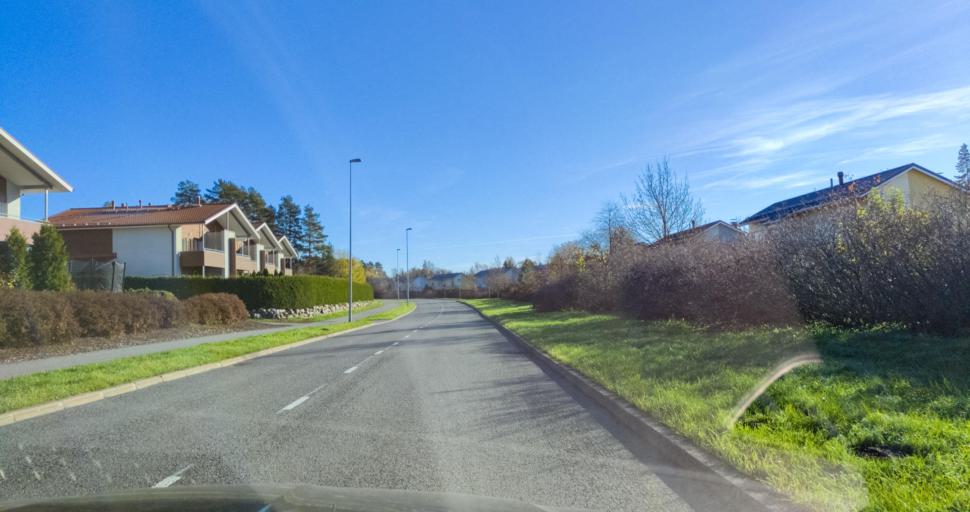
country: FI
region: Varsinais-Suomi
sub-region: Turku
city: Turku
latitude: 60.4098
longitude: 22.2162
